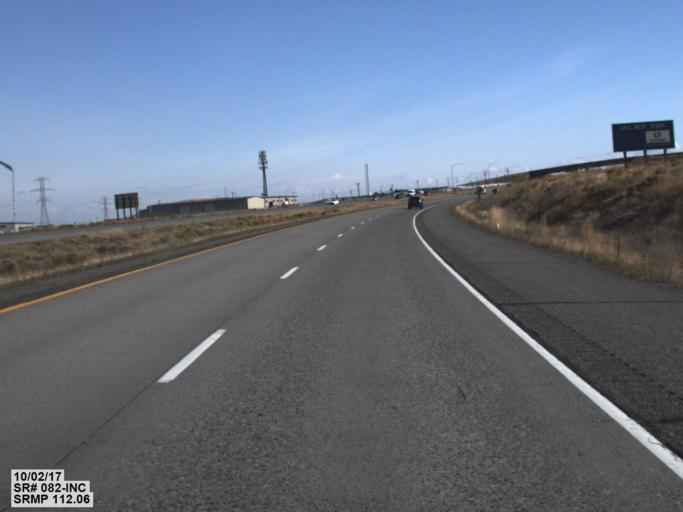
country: US
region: Washington
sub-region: Franklin County
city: West Pasco
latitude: 46.1732
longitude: -119.2124
